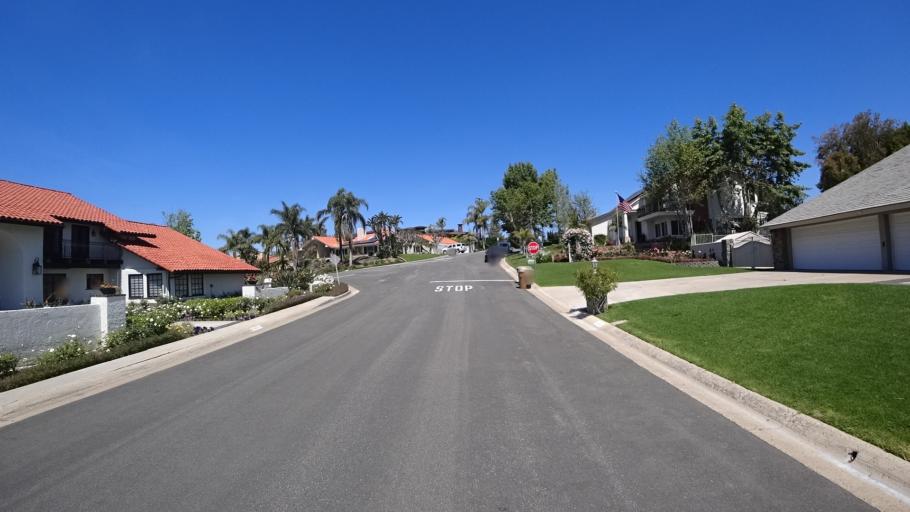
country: US
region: California
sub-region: Orange County
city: Villa Park
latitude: 33.8211
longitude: -117.7974
